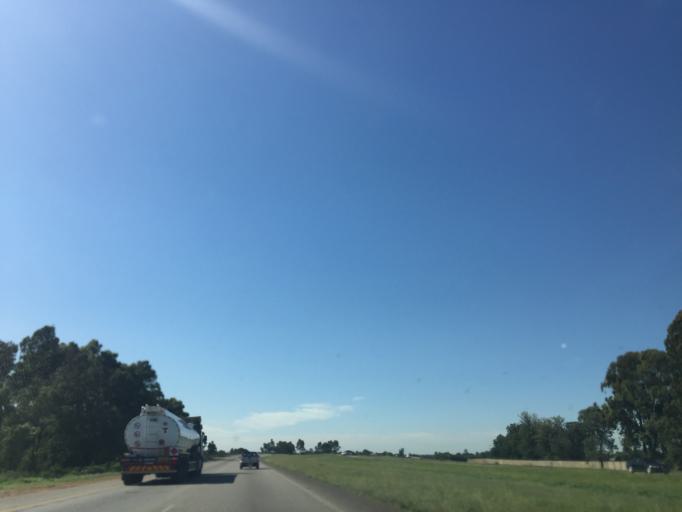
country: ZA
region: Gauteng
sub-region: Sedibeng District Municipality
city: Meyerton
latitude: -26.5693
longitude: 27.9985
